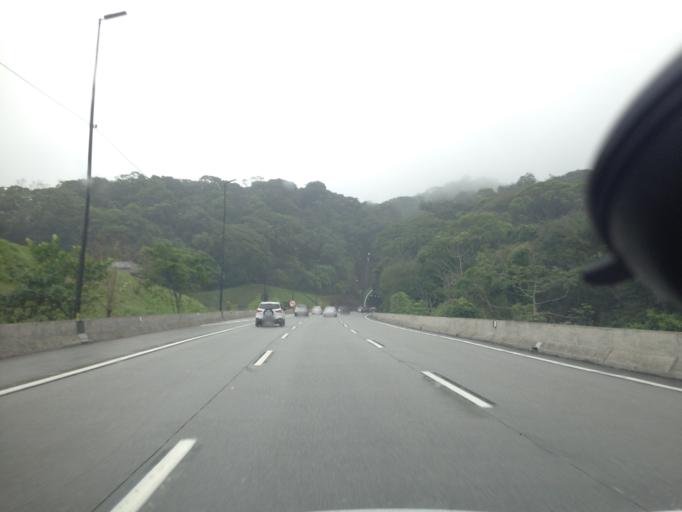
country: BR
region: Sao Paulo
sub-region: Cubatao
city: Cubatao
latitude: -23.8978
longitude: -46.4734
